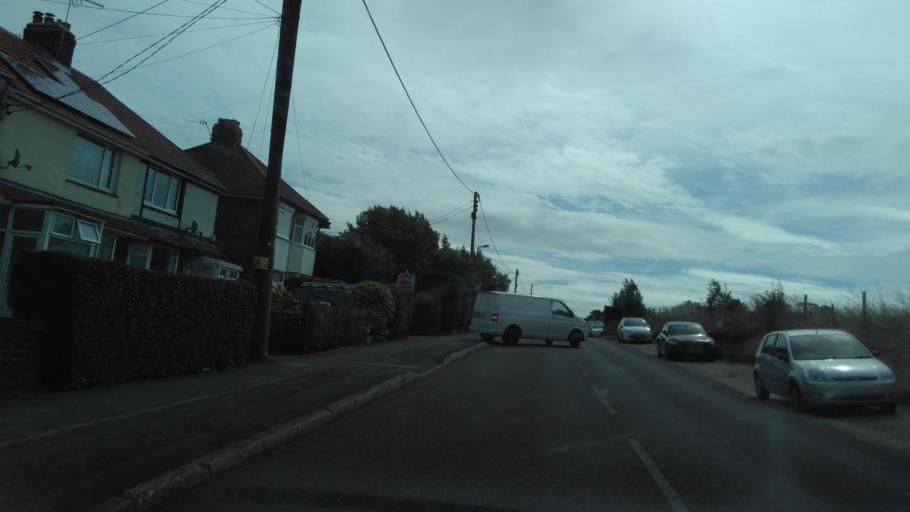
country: GB
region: England
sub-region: Kent
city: Chartham
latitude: 51.2496
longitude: 1.0158
